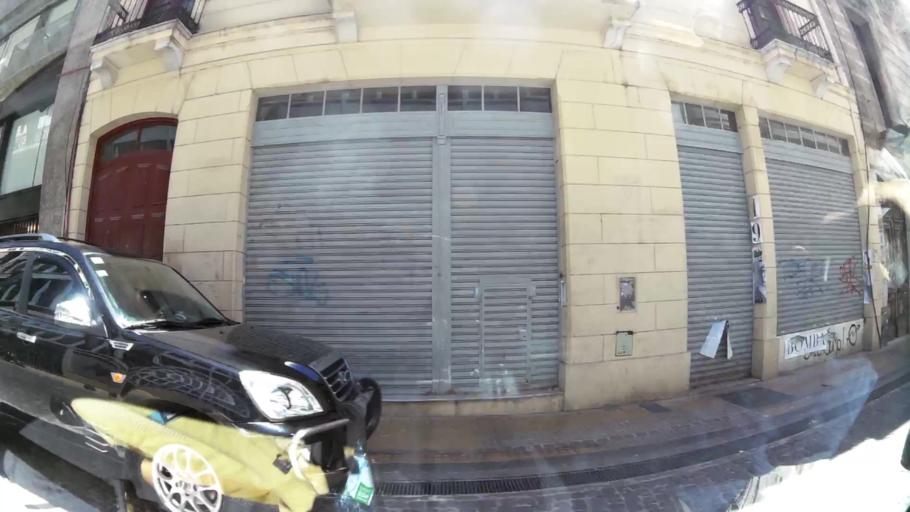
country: AR
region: Buenos Aires F.D.
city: Buenos Aires
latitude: -34.6102
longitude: -58.3729
